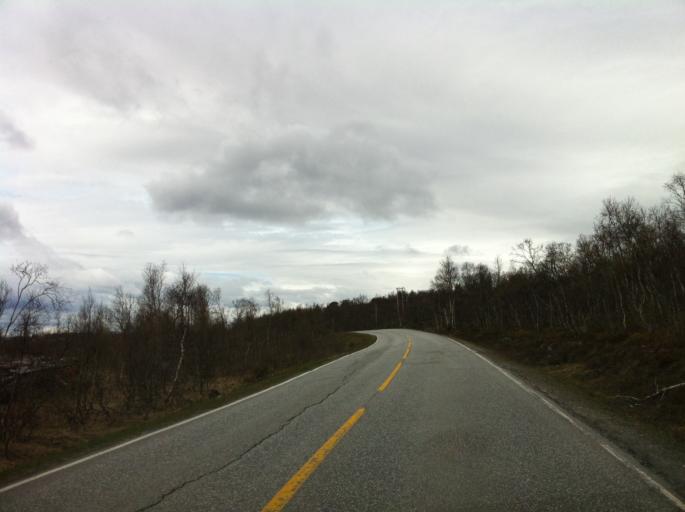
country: NO
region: Sor-Trondelag
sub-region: Roros
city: Roros
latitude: 62.5996
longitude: 11.4917
